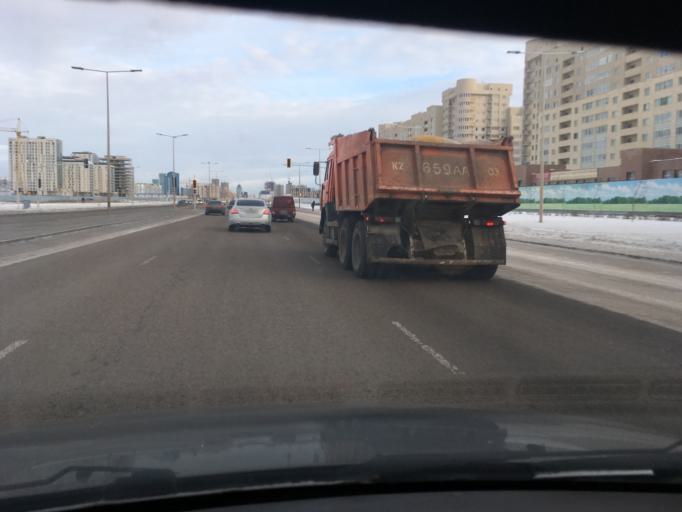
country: KZ
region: Astana Qalasy
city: Astana
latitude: 51.1305
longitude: 71.3768
